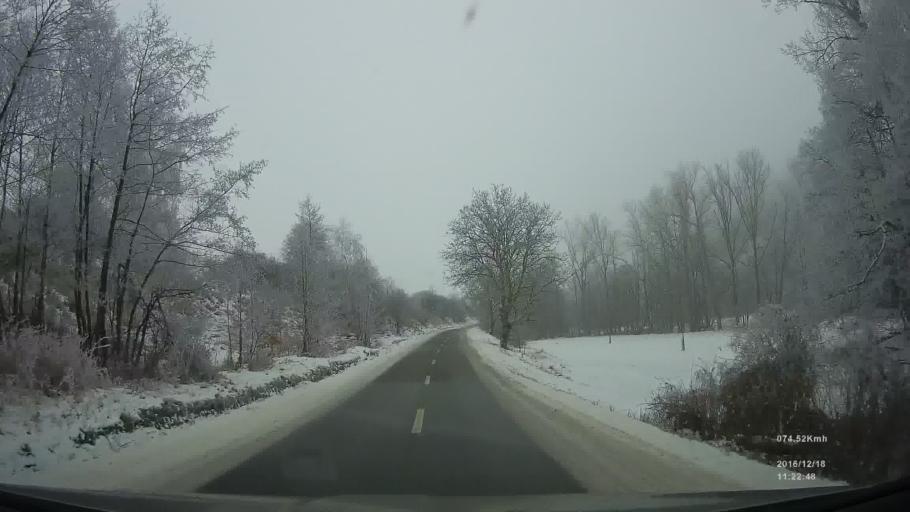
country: SK
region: Presovsky
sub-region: Okres Presov
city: Presov
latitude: 48.8993
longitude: 21.3824
